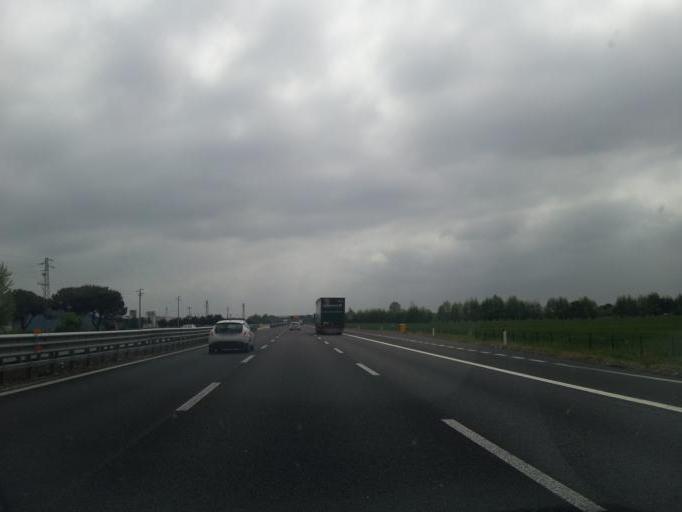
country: IT
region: Veneto
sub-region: Provincia di Vicenza
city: Torri di Quartesolo
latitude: 45.4986
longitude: 11.6445
